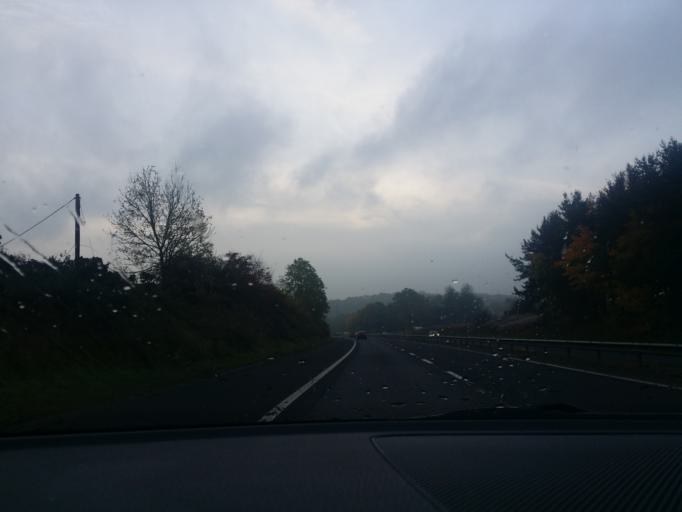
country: GB
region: Scotland
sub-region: Stirling
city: Bannockburn
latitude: 56.0725
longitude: -3.9046
